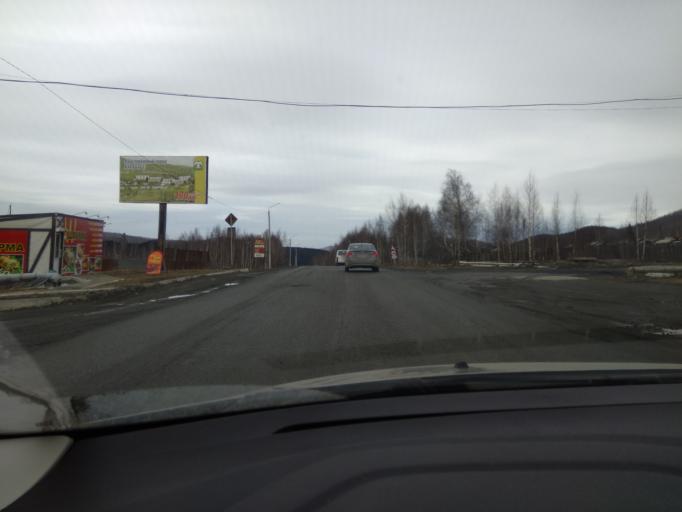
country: RU
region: Chelyabinsk
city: Karabash
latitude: 55.4896
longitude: 60.2406
